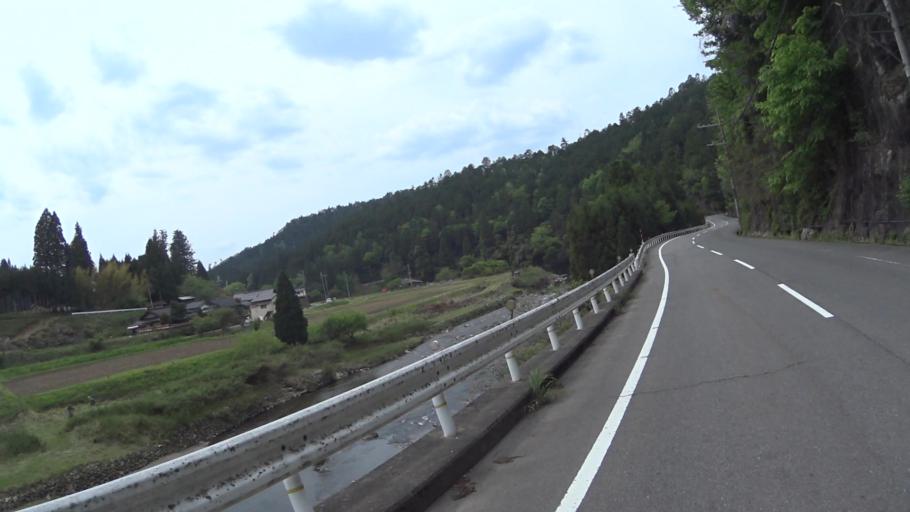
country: JP
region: Kyoto
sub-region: Kyoto-shi
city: Kamigyo-ku
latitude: 35.1973
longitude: 135.7041
